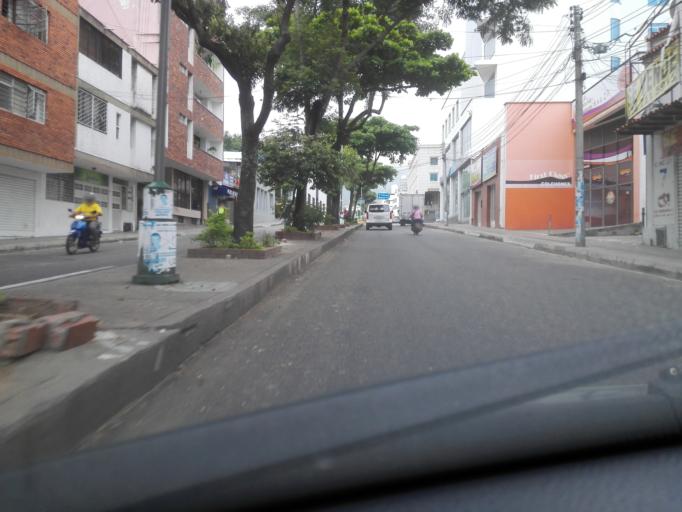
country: CO
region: Santander
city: Bucaramanga
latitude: 7.1208
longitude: -73.1181
